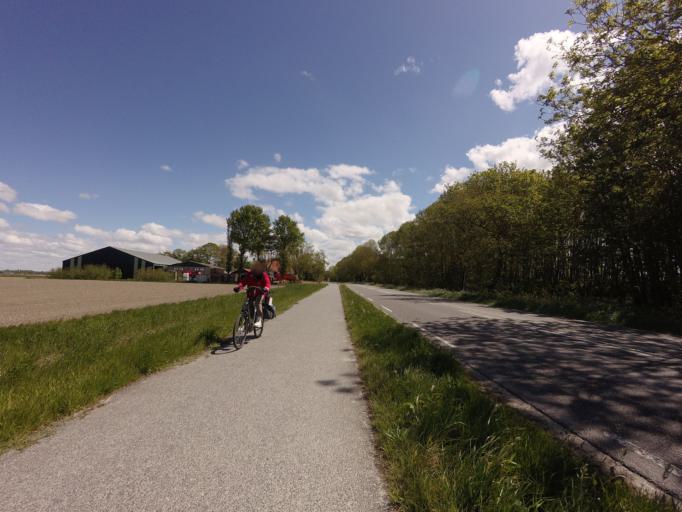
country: NL
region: Friesland
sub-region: Gemeente Harlingen
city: Harlingen
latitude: 53.1373
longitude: 5.4534
